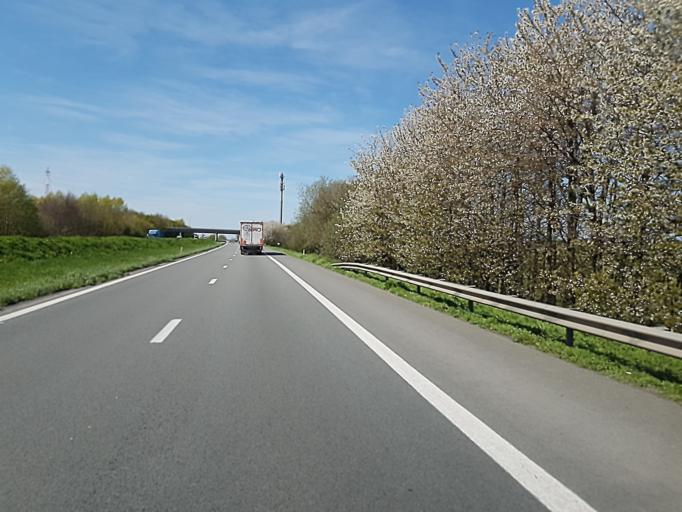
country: BE
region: Wallonia
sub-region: Province du Hainaut
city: Estaimpuis
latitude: 50.7632
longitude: 3.2845
